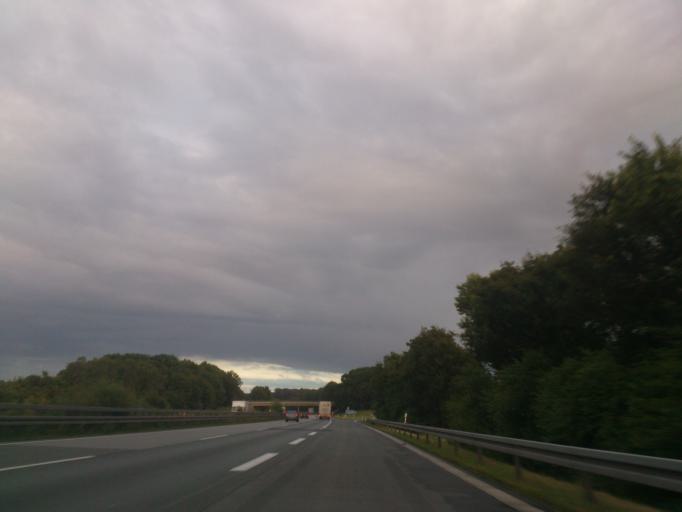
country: DE
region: North Rhine-Westphalia
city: Marsberg
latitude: 51.5417
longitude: 8.8340
